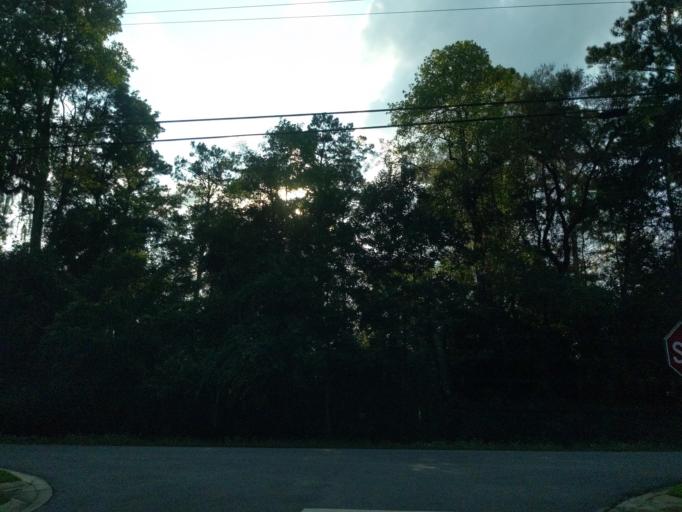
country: US
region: Georgia
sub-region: Thomas County
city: Thomasville
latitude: 30.8985
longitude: -83.9464
